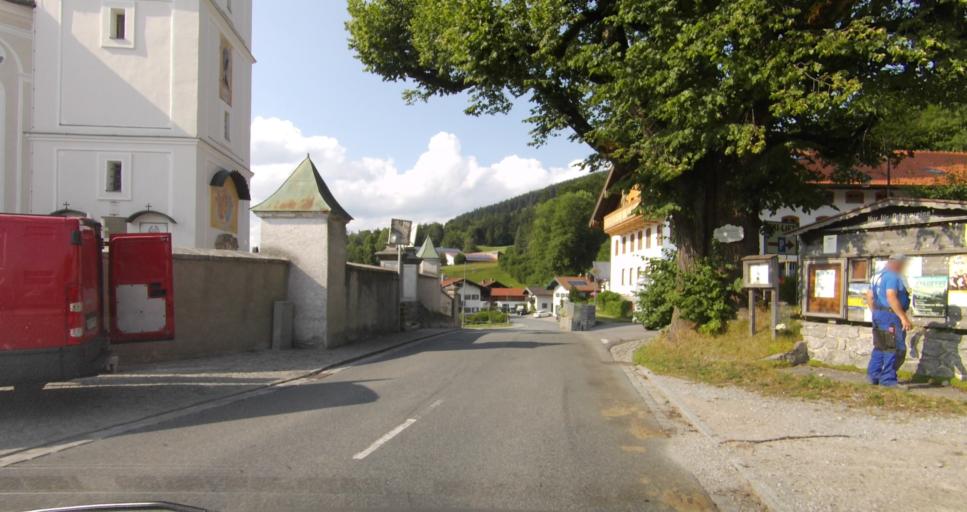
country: DE
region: Bavaria
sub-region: Upper Bavaria
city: Fischbachau
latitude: 47.7415
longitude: 11.9522
